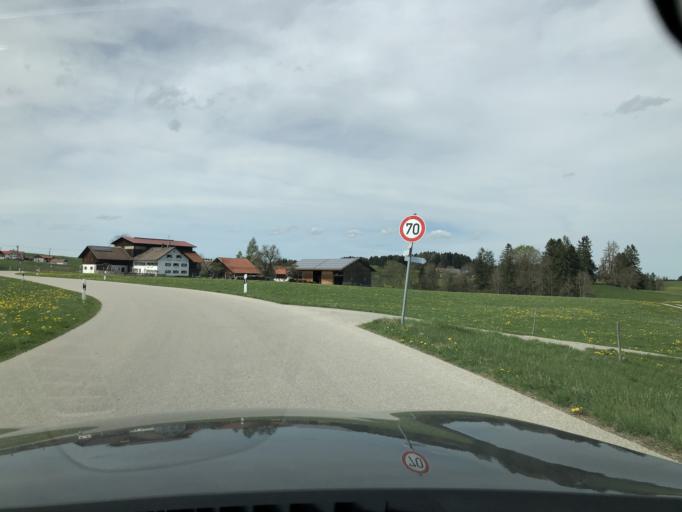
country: DE
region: Bavaria
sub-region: Swabia
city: Wald
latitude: 47.7051
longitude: 10.5609
